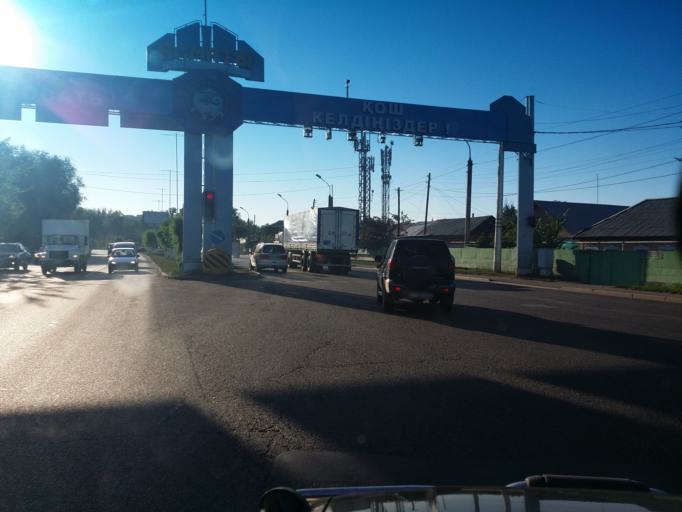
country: KZ
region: Almaty Oblysy
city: Pervomayskiy
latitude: 43.3437
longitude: 76.9946
